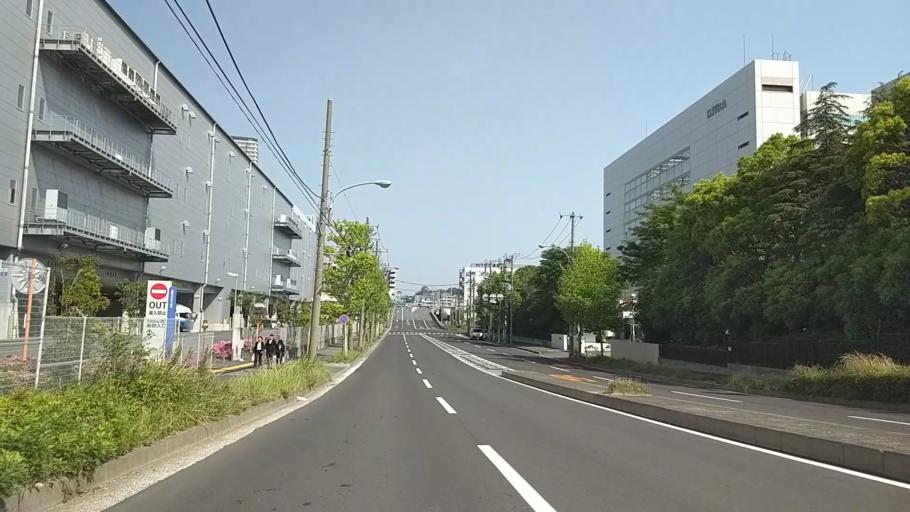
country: JP
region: Kanagawa
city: Yokohama
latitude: 35.4830
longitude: 139.6566
